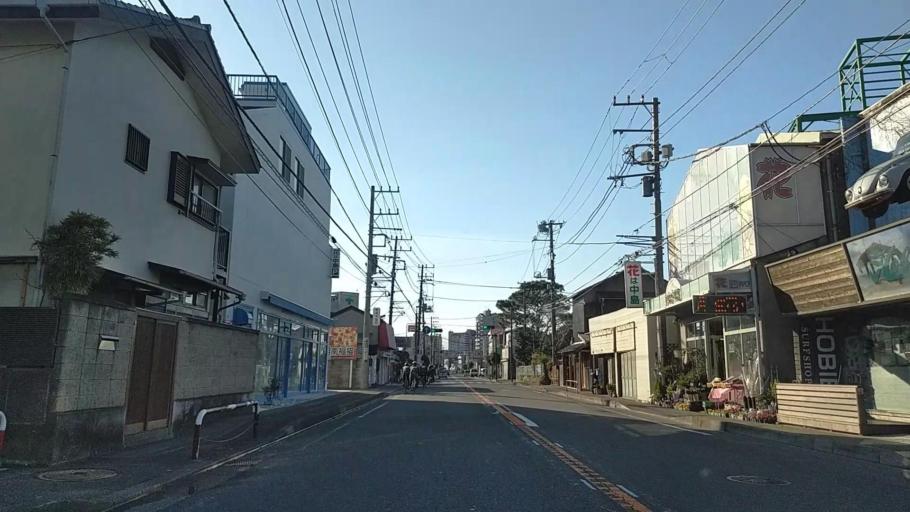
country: JP
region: Kanagawa
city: Fujisawa
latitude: 35.3175
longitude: 139.4857
